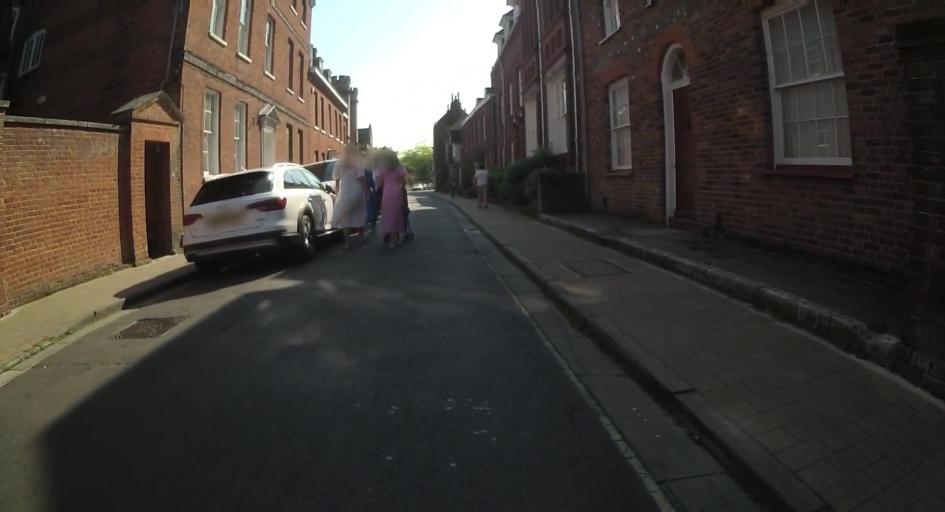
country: GB
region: England
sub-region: Hampshire
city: Winchester
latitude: 51.0578
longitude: -1.3152
